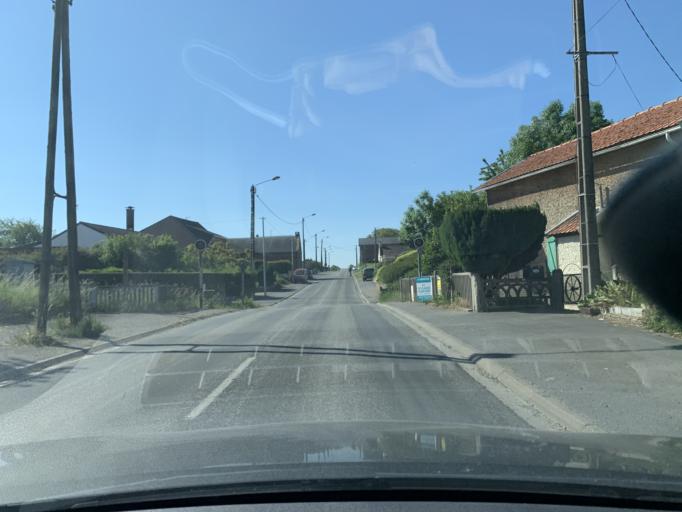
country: FR
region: Nord-Pas-de-Calais
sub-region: Departement du Nord
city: Cambrai
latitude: 50.1556
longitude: 3.2420
